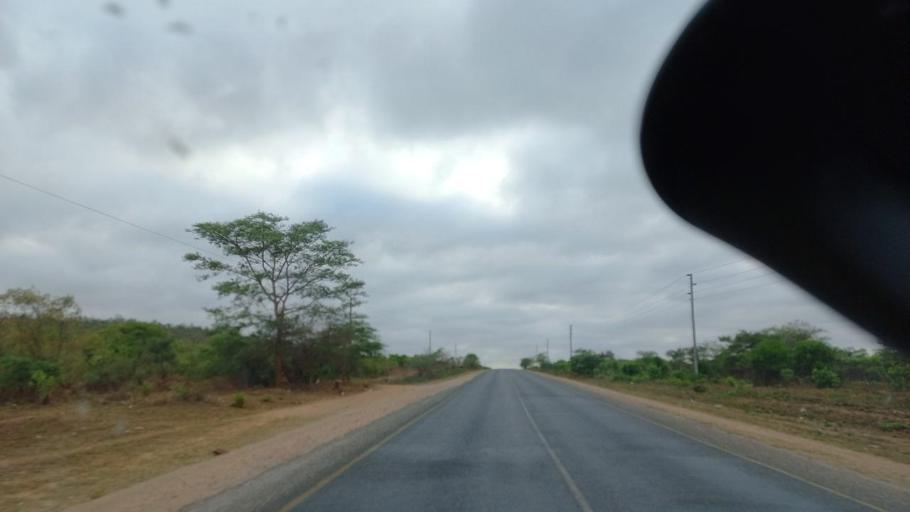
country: ZM
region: Lusaka
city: Chongwe
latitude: -15.3419
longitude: 28.5970
